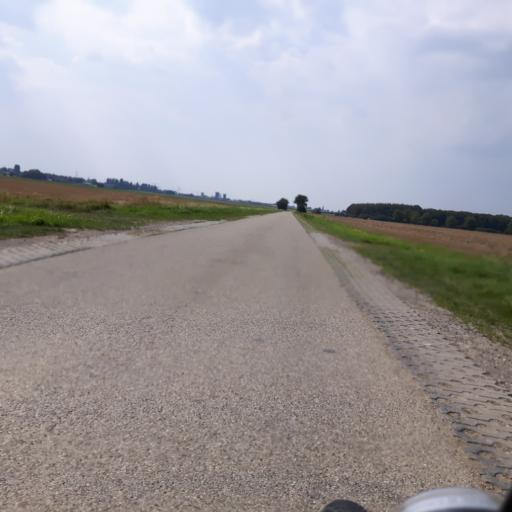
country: NL
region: Zeeland
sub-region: Gemeente Reimerswaal
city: Yerseke
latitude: 51.4818
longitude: 3.9890
